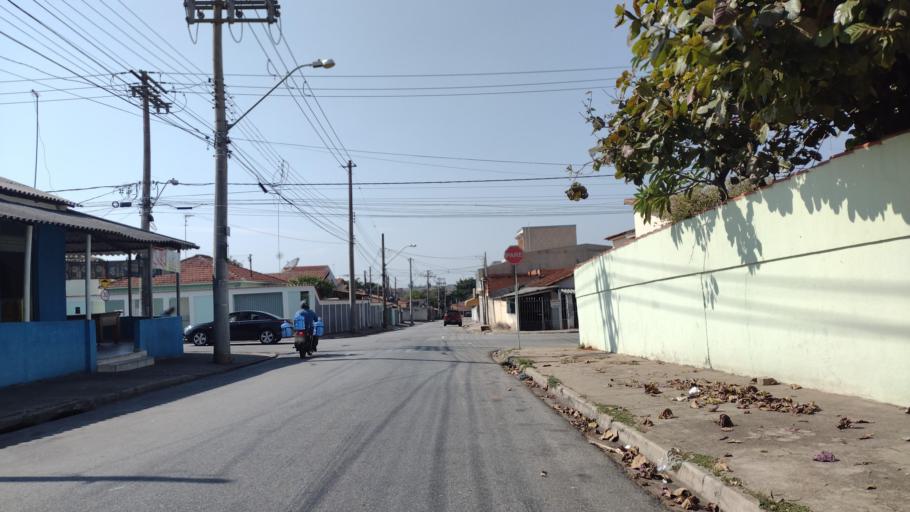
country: BR
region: Sao Paulo
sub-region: Sorocaba
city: Sorocaba
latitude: -23.4181
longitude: -47.4120
